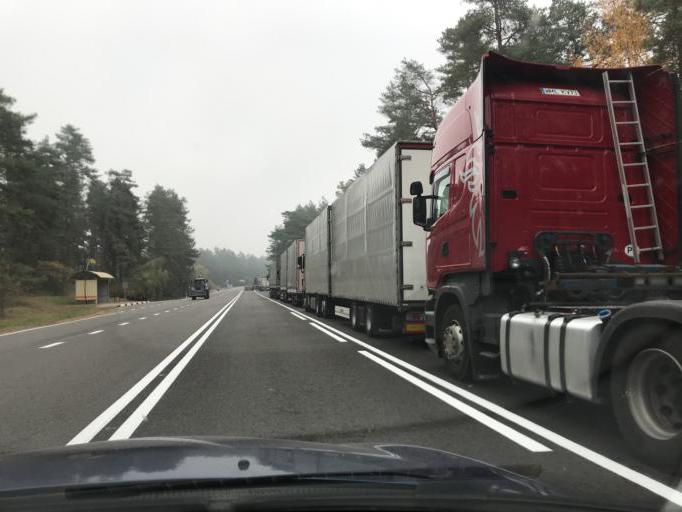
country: LT
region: Alytaus apskritis
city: Druskininkai
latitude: 53.9282
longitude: 23.9362
